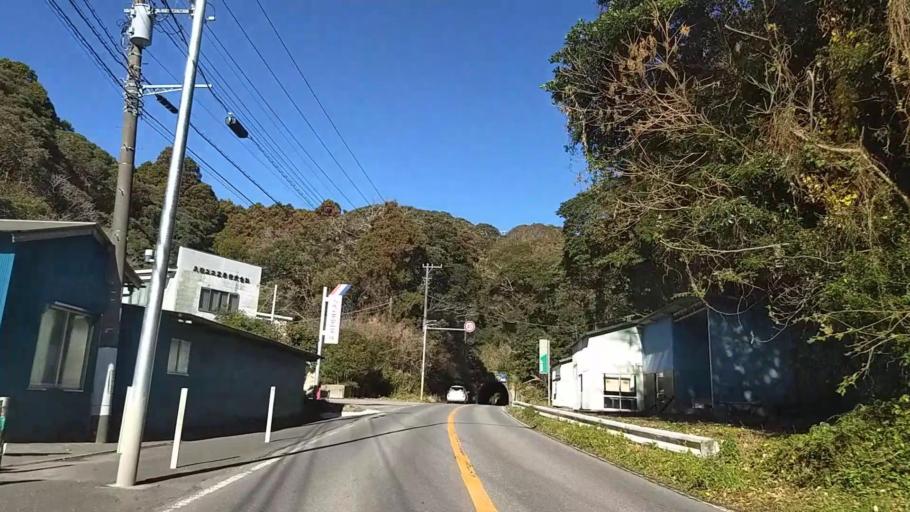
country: JP
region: Chiba
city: Katsuura
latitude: 35.1608
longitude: 140.3270
